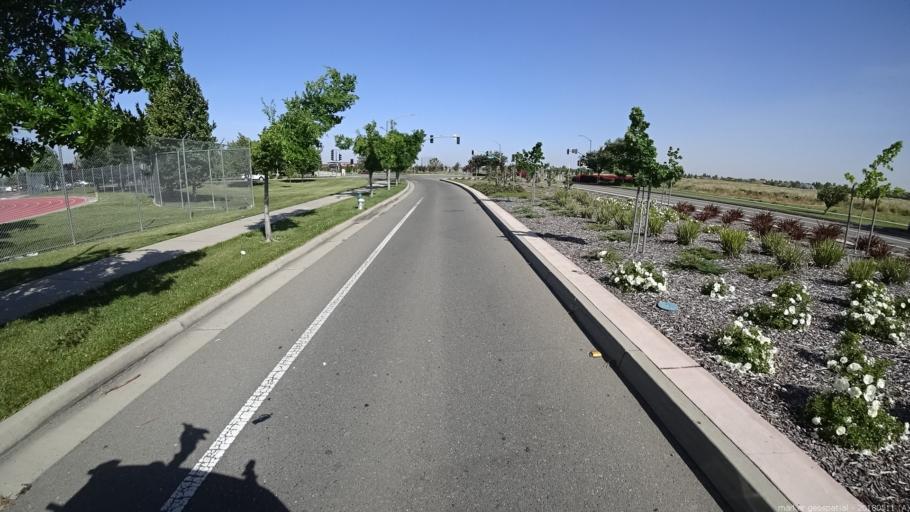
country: US
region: California
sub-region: Sacramento County
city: Rio Linda
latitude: 38.6597
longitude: -121.5148
